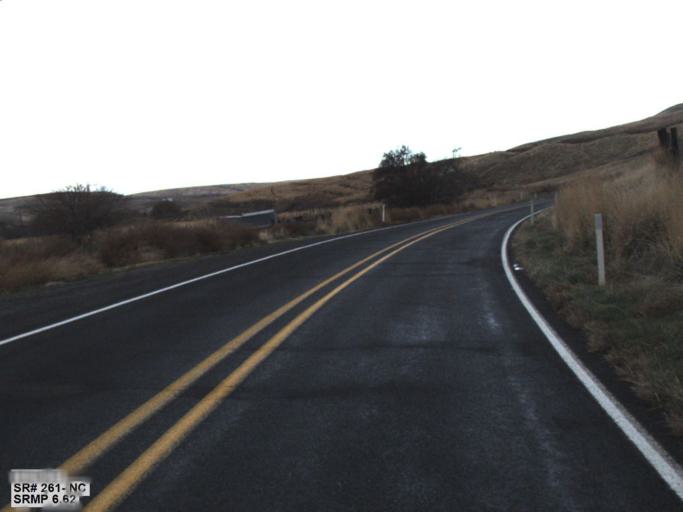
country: US
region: Washington
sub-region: Columbia County
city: Dayton
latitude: 46.5113
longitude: -118.1015
